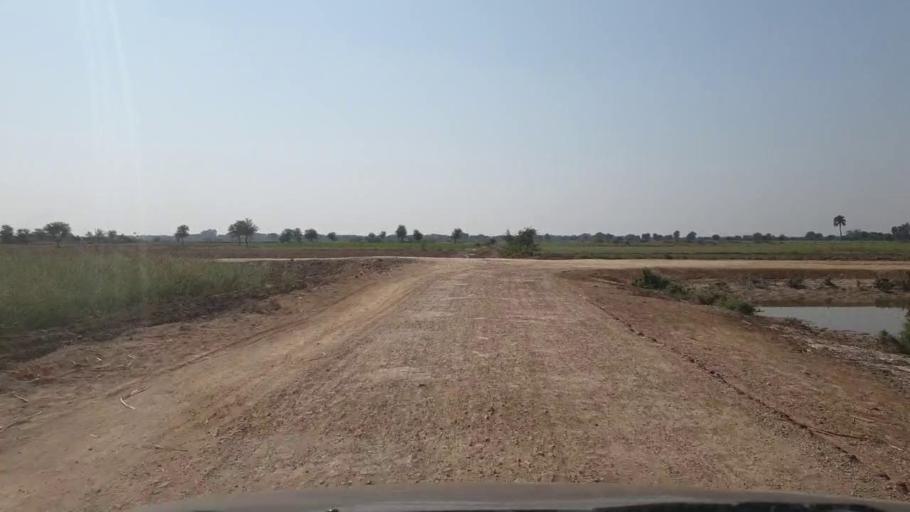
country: PK
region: Sindh
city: Samaro
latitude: 25.2325
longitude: 69.2810
